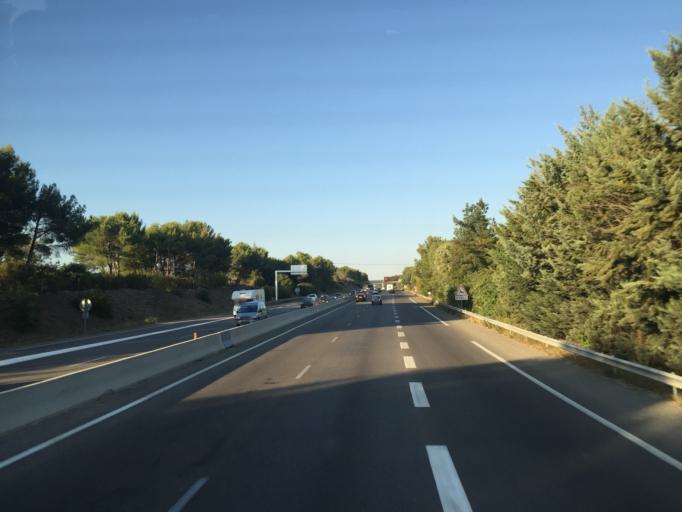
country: FR
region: Provence-Alpes-Cote d'Azur
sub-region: Departement des Bouches-du-Rhone
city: Venelles
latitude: 43.5943
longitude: 5.4855
